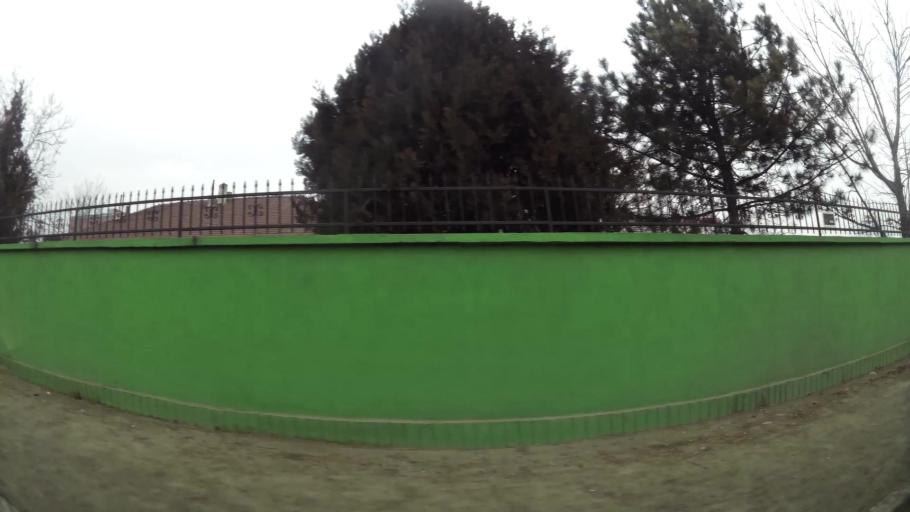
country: MK
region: Cair
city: Cair
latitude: 41.9970
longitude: 21.4815
